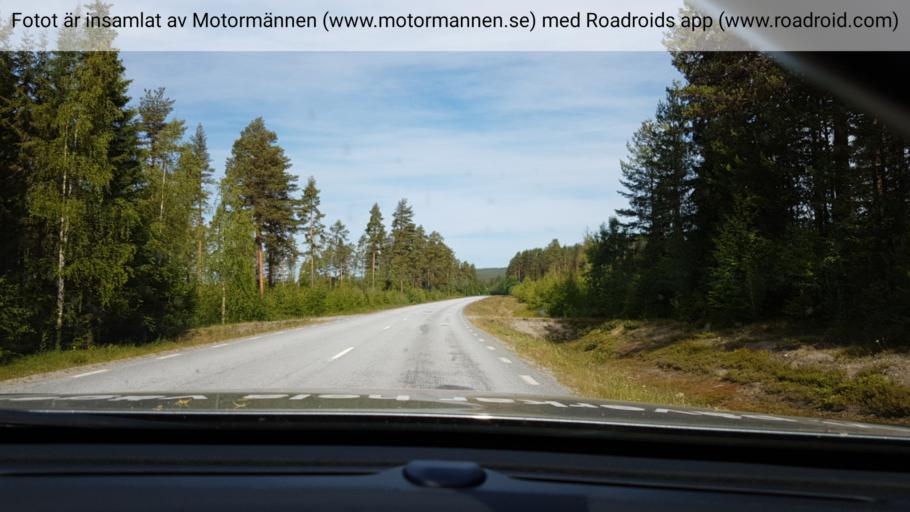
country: SE
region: Vaesterbotten
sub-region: Asele Kommun
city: Asele
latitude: 64.1792
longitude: 17.2808
